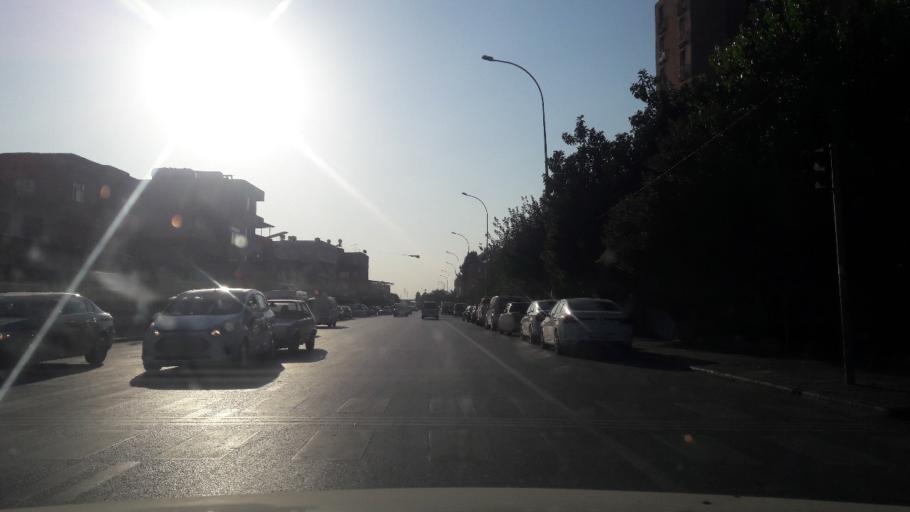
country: TR
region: Adana
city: Seyhan
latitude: 36.9874
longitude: 35.3031
